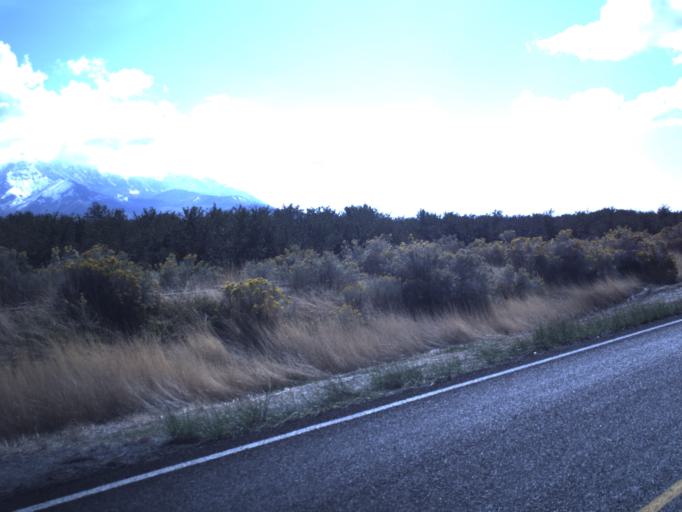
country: US
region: Utah
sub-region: Utah County
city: West Mountain
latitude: 40.0195
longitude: -111.7875
